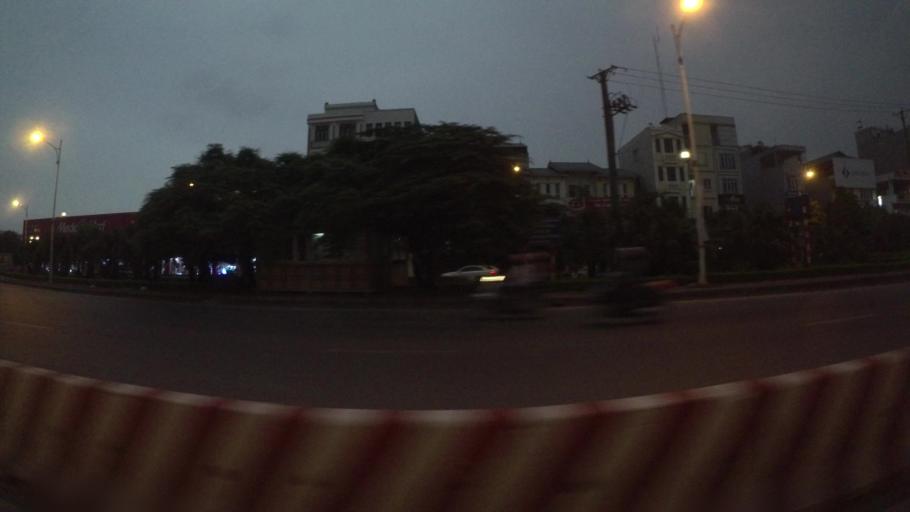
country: VN
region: Ha Noi
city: Trau Quy
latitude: 21.0256
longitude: 105.8954
